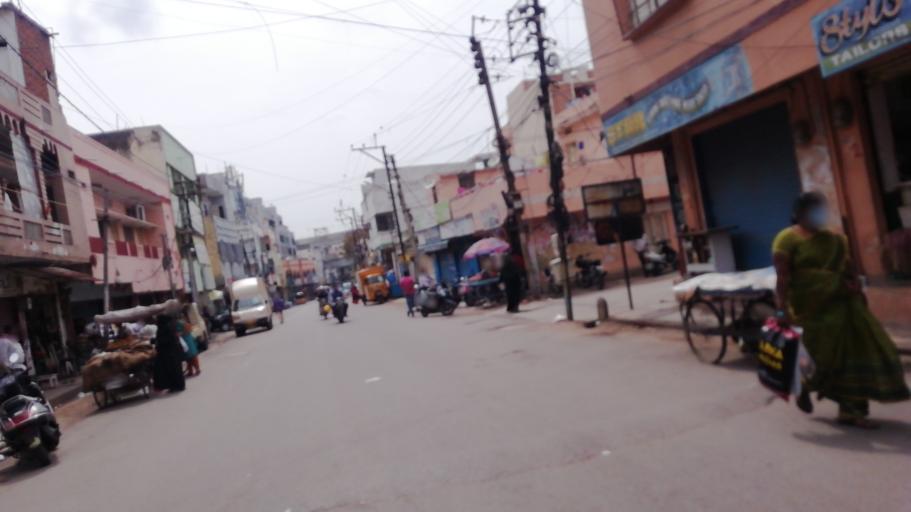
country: IN
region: Telangana
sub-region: Hyderabad
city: Malkajgiri
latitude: 17.4149
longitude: 78.5005
